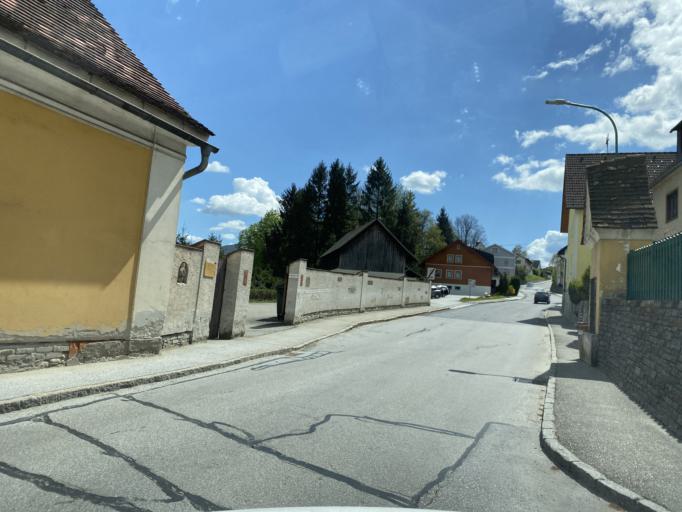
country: AT
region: Styria
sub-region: Politischer Bezirk Weiz
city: Birkfeld
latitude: 47.3535
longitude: 15.6933
